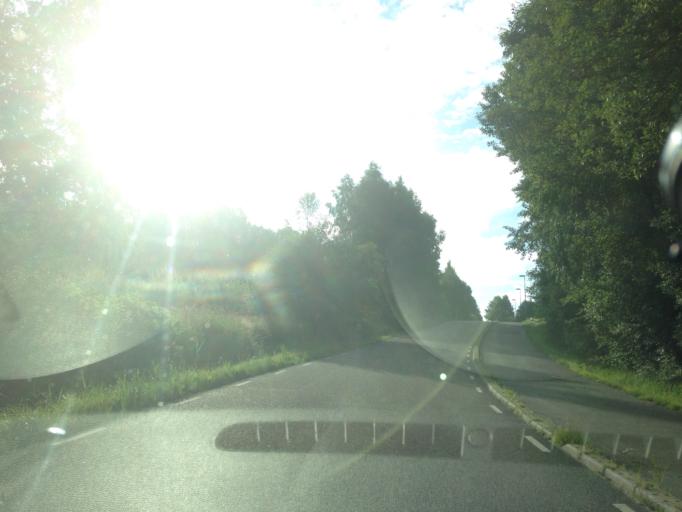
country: SE
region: Vaestra Goetaland
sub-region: Goteborg
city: Goeteborg
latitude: 57.7677
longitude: 11.9443
